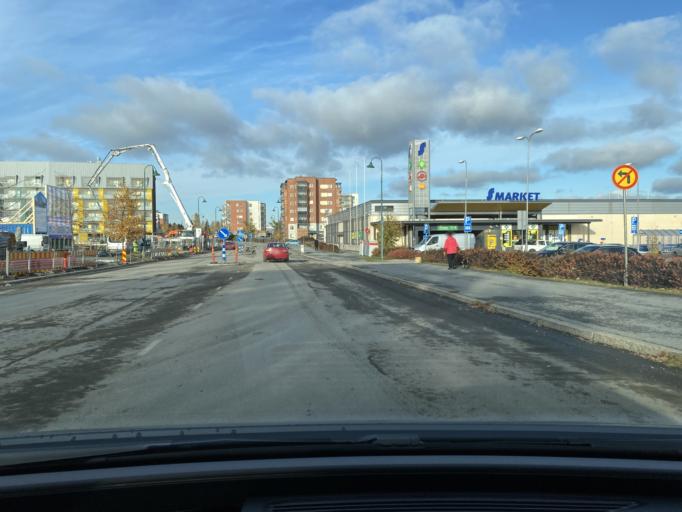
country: FI
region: Pirkanmaa
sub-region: Tampere
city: Lempaeaelae
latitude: 61.3129
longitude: 23.7588
